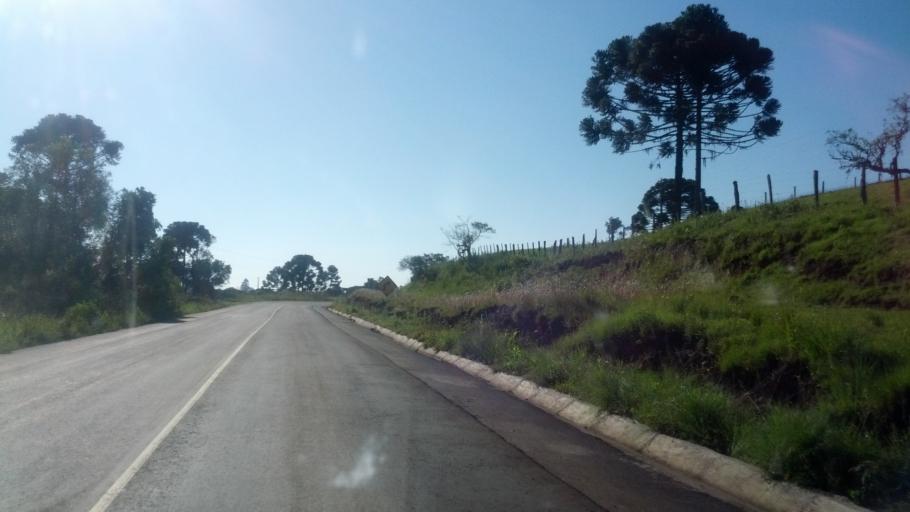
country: BR
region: Santa Catarina
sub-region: Lages
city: Lages
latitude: -27.9307
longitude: -50.5307
